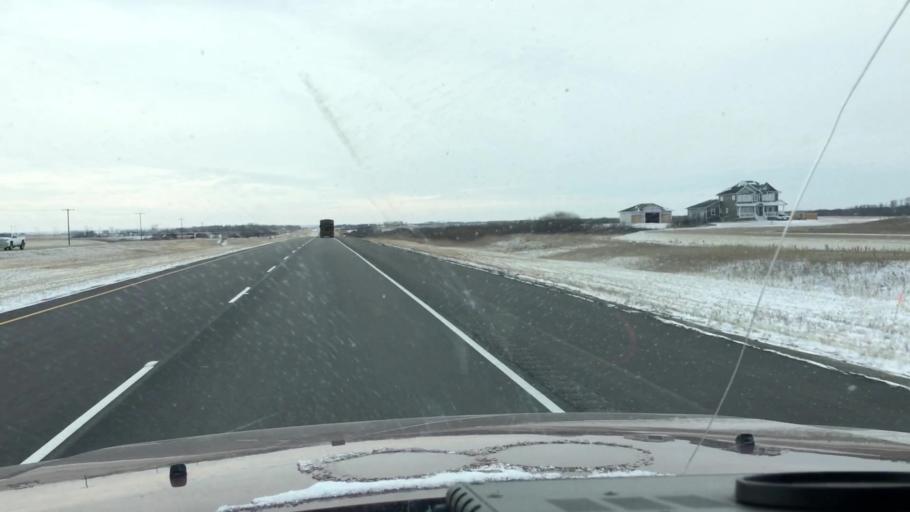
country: CA
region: Saskatchewan
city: Saskatoon
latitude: 51.9289
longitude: -106.5348
